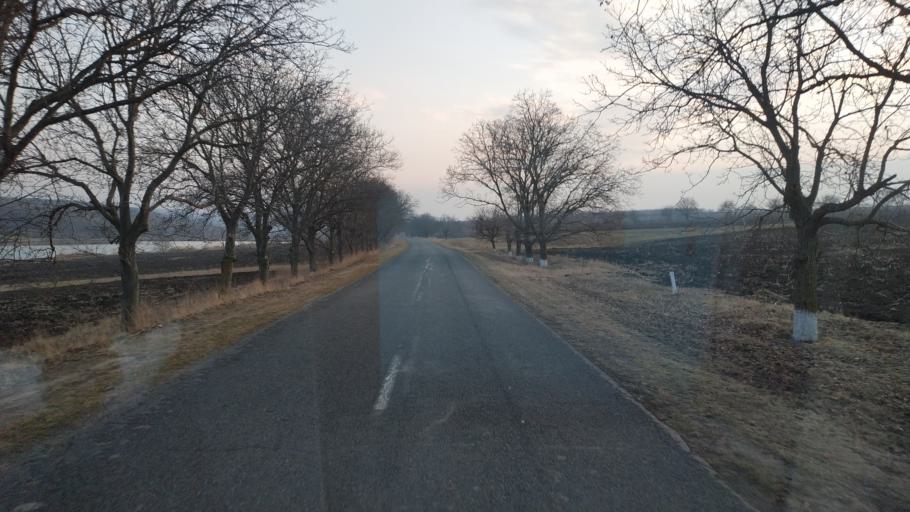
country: MD
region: Hincesti
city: Dancu
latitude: 46.7001
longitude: 28.3375
